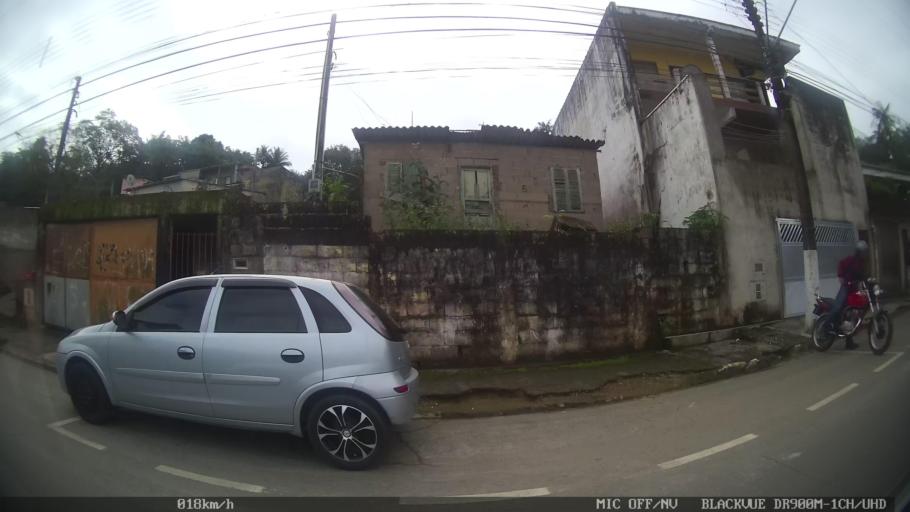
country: BR
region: Sao Paulo
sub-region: Cajati
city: Cajati
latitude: -24.7267
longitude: -48.1082
